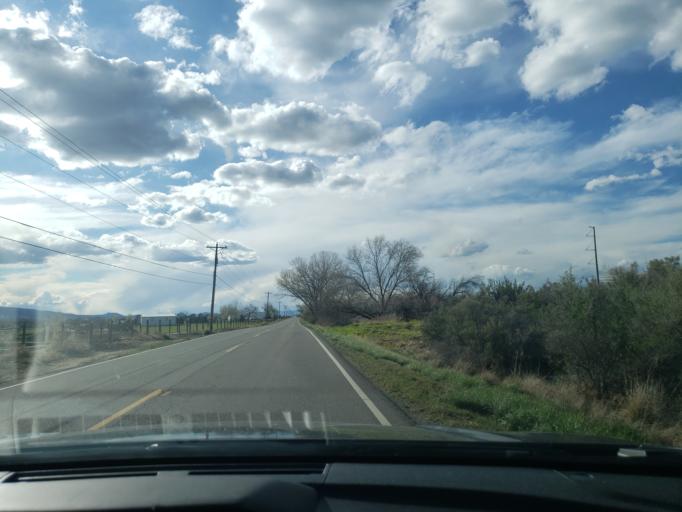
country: US
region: Colorado
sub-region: Mesa County
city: Redlands
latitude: 39.1228
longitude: -108.6712
